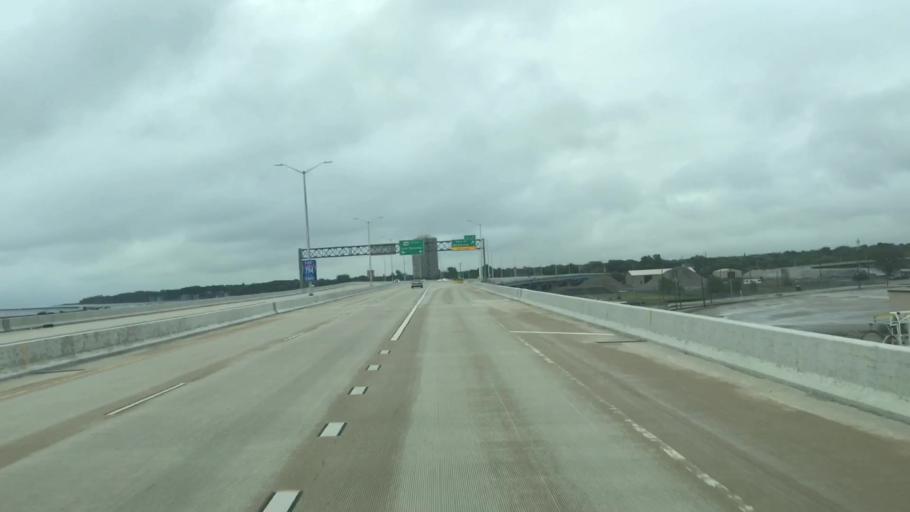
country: US
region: Wisconsin
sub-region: Milwaukee County
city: Milwaukee
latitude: 43.0102
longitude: -87.8933
